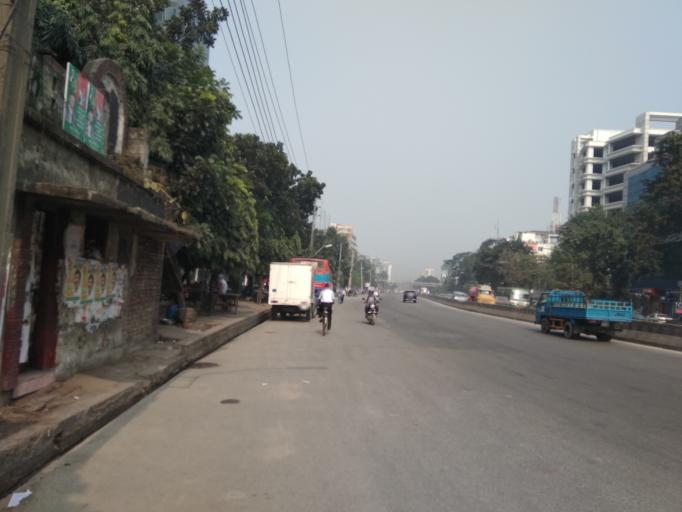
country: BD
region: Dhaka
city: Tungi
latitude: 23.8618
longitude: 90.3999
